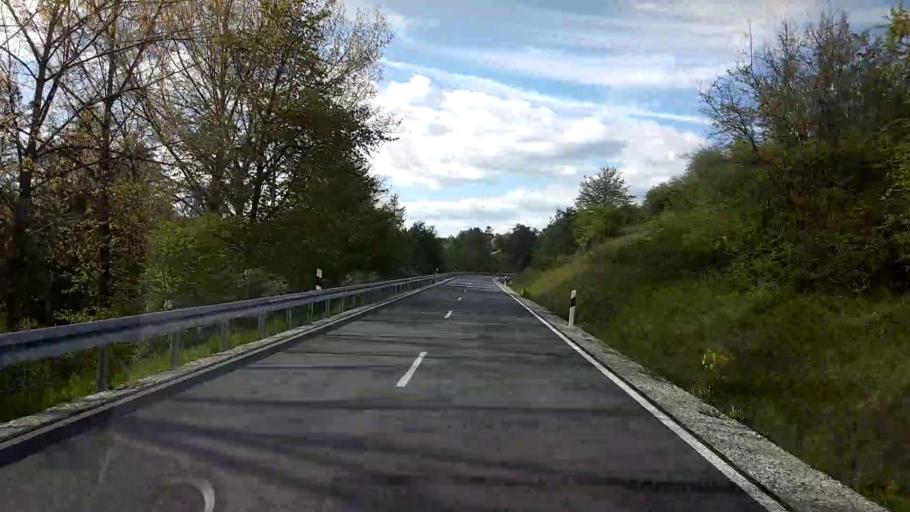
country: DE
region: Bavaria
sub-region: Upper Franconia
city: Hollfeld
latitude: 49.9469
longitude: 11.2829
